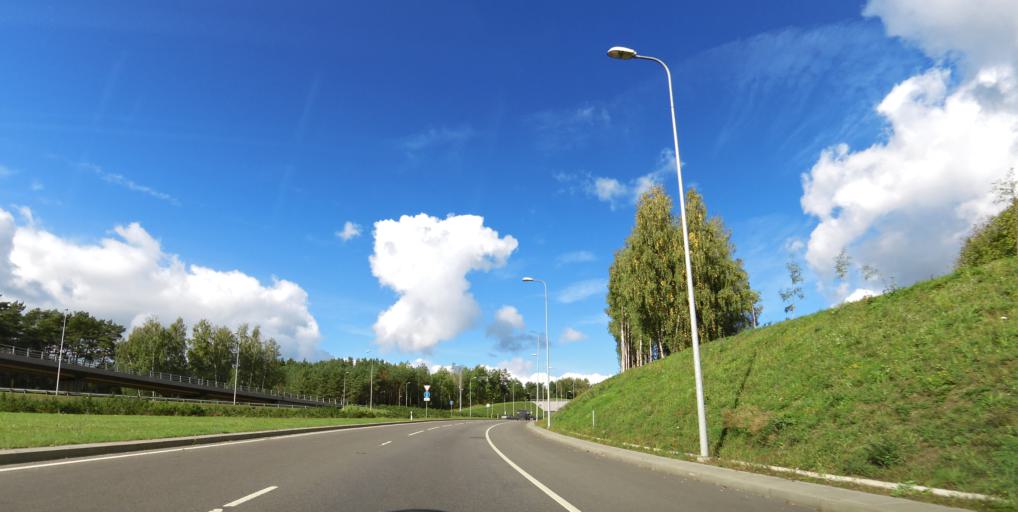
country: LT
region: Vilnius County
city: Lazdynai
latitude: 54.6721
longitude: 25.1974
